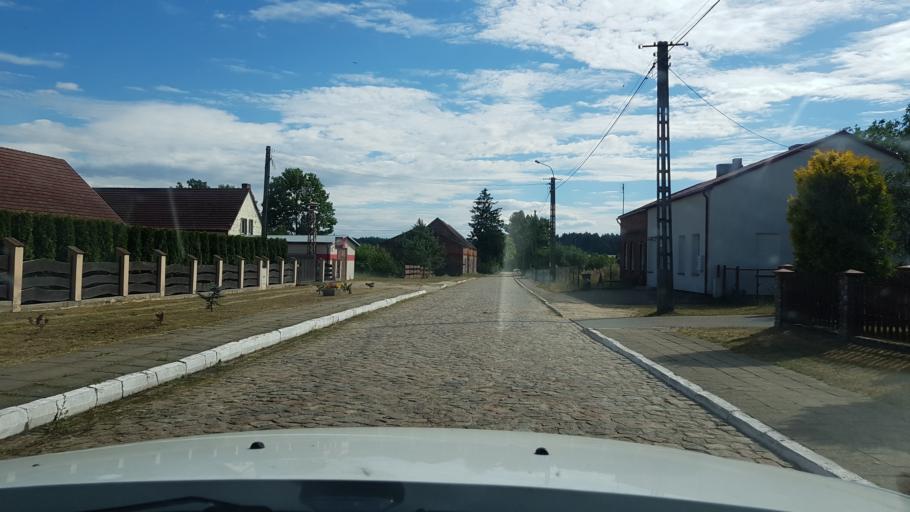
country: PL
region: West Pomeranian Voivodeship
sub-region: Powiat drawski
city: Zlocieniec
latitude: 53.6346
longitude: 16.0373
